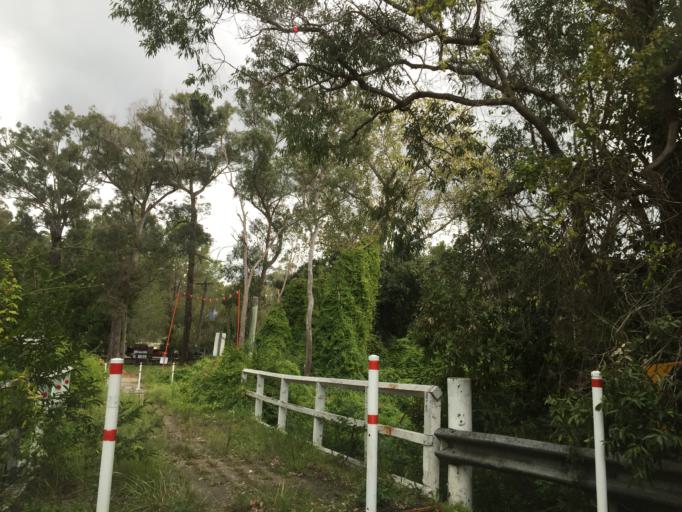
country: AU
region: New South Wales
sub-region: The Hills Shire
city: Beaumont Hills
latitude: -33.6928
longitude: 150.9689
